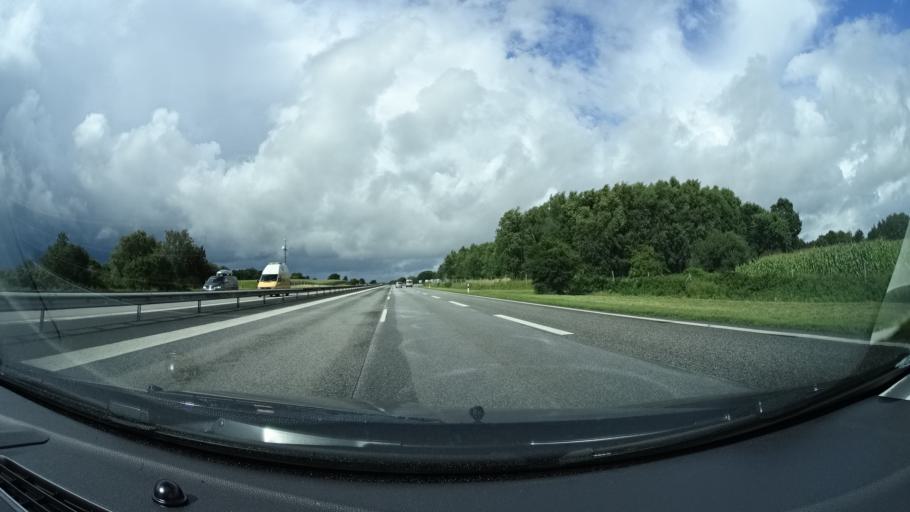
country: DE
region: Schleswig-Holstein
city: Lottorf
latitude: 54.4411
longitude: 9.5908
